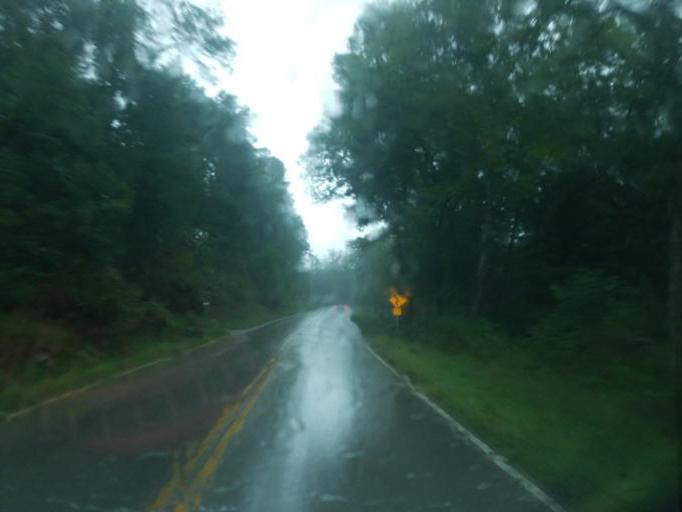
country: US
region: Kentucky
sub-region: Carter County
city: Olive Hill
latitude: 38.3391
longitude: -83.2011
